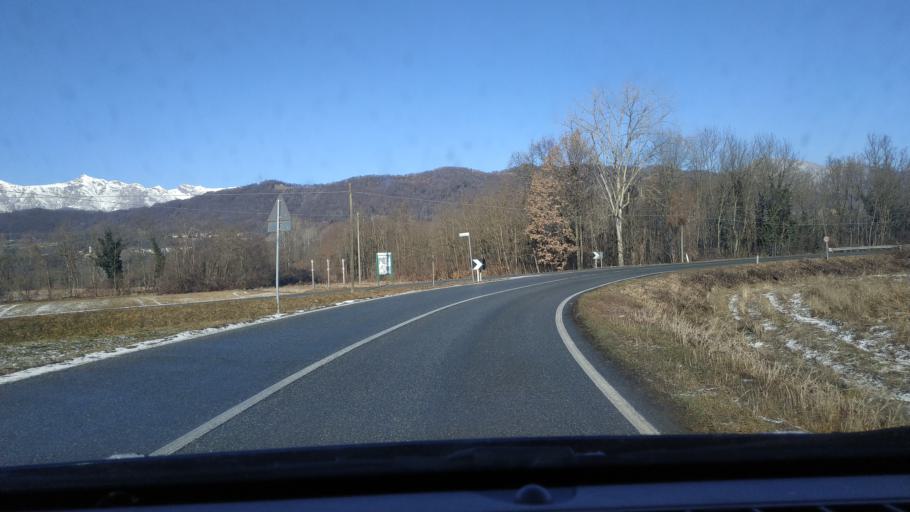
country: IT
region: Piedmont
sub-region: Provincia di Torino
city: Parella
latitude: 45.4183
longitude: 7.7973
